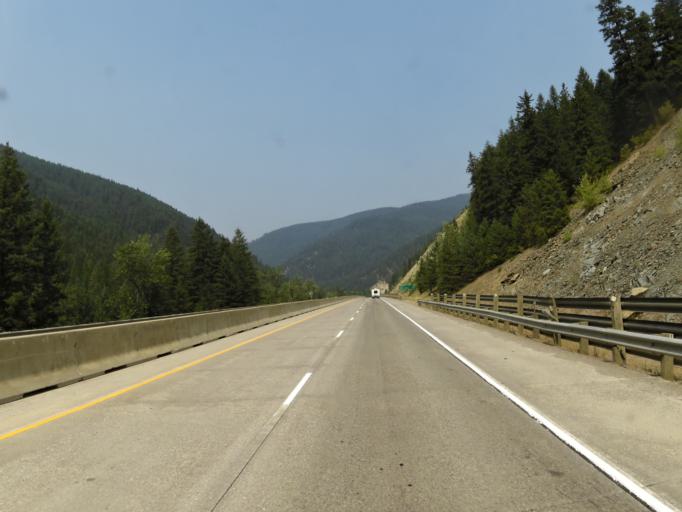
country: US
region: Montana
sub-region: Sanders County
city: Thompson Falls
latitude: 47.3035
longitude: -115.2020
